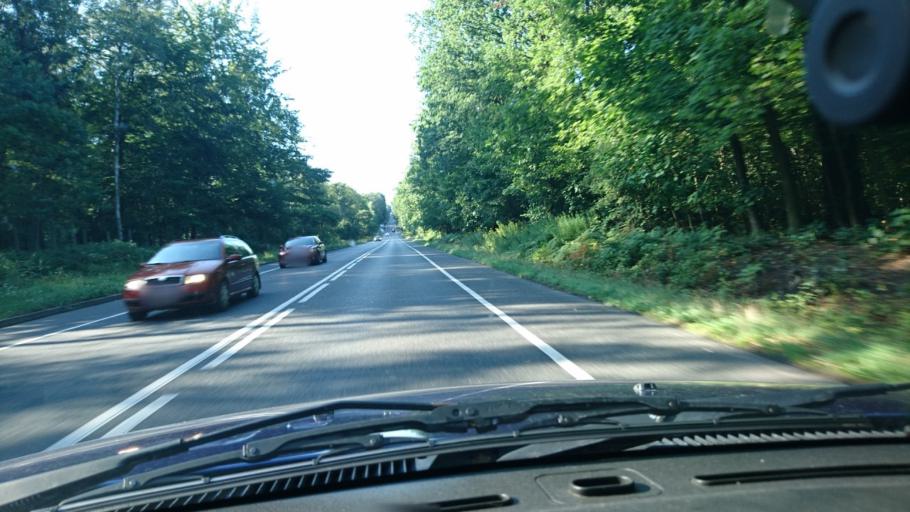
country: PL
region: Silesian Voivodeship
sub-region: Gliwice
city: Gliwice
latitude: 50.3263
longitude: 18.6606
